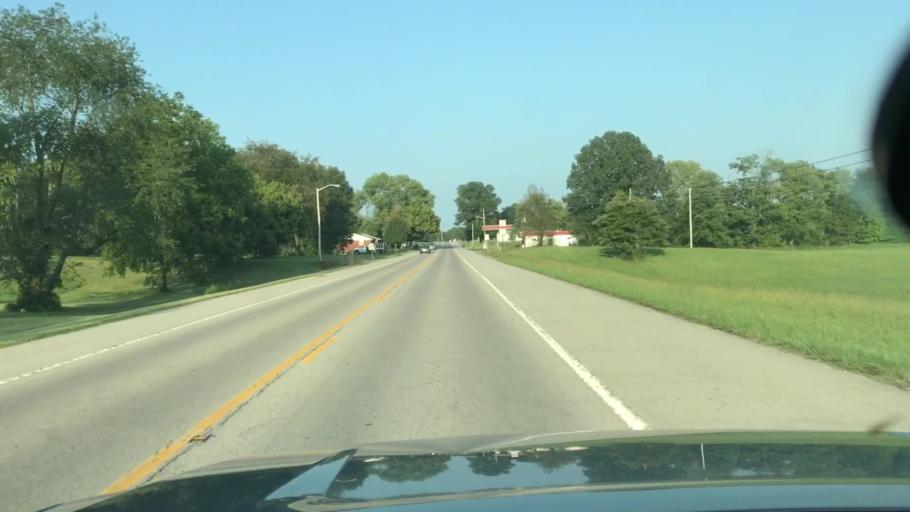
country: US
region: Tennessee
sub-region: Sumner County
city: Portland
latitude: 36.5778
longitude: -86.4409
